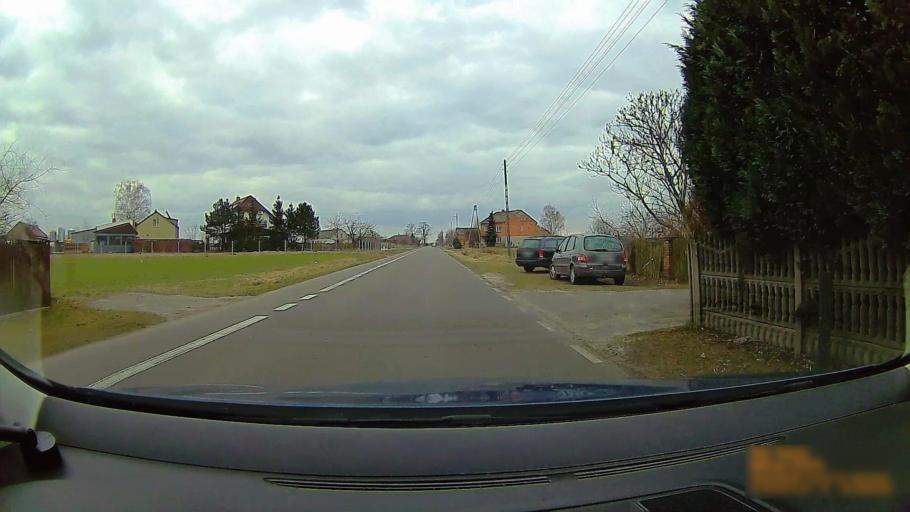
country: PL
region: Greater Poland Voivodeship
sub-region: Powiat koninski
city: Rzgow Pierwszy
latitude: 52.1198
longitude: 18.0692
